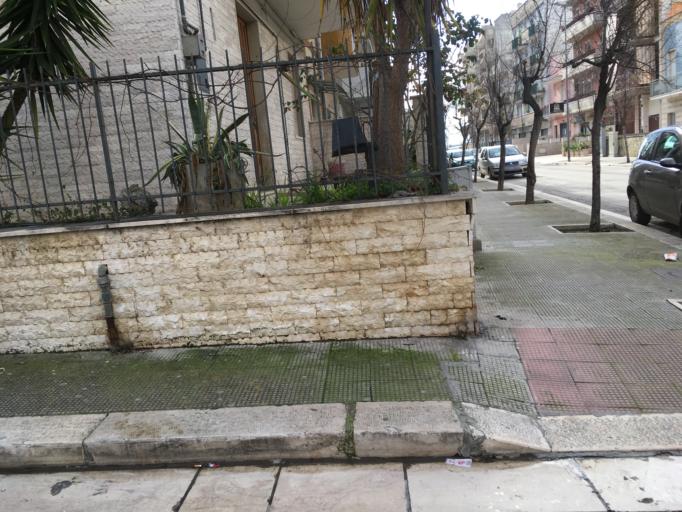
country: IT
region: Apulia
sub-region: Provincia di Barletta - Andria - Trani
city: Andria
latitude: 41.2192
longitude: 16.2996
